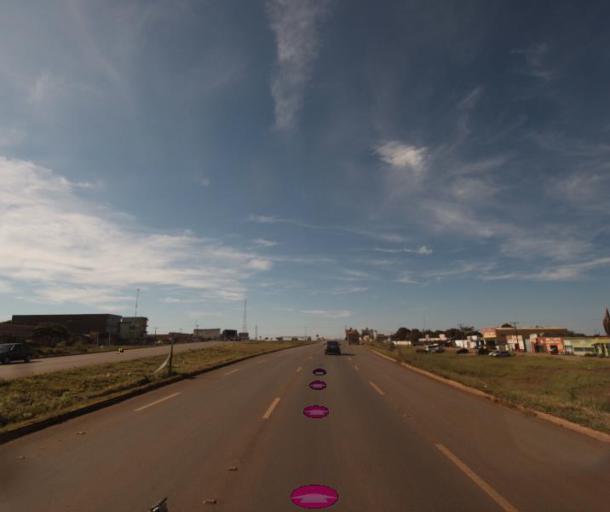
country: BR
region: Federal District
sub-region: Brasilia
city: Brasilia
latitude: -15.7477
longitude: -48.2642
